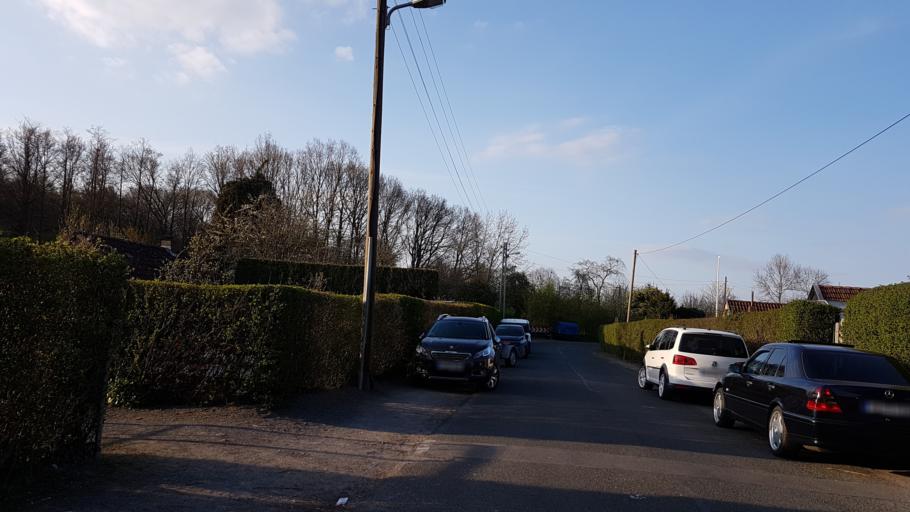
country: DE
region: Lower Saxony
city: Ronnenberg
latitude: 52.3522
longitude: 9.6845
